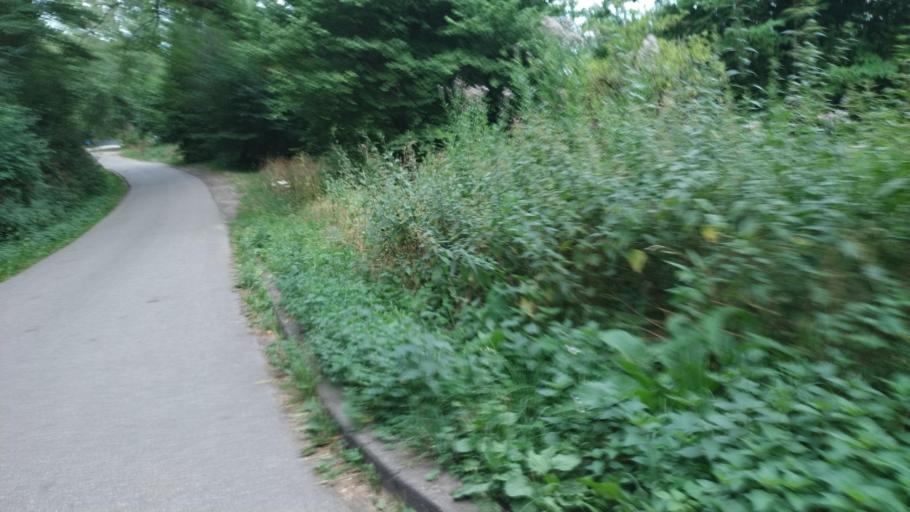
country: DE
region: Baden-Wuerttemberg
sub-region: Karlsruhe Region
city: Weingarten
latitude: 49.0382
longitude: 8.4736
